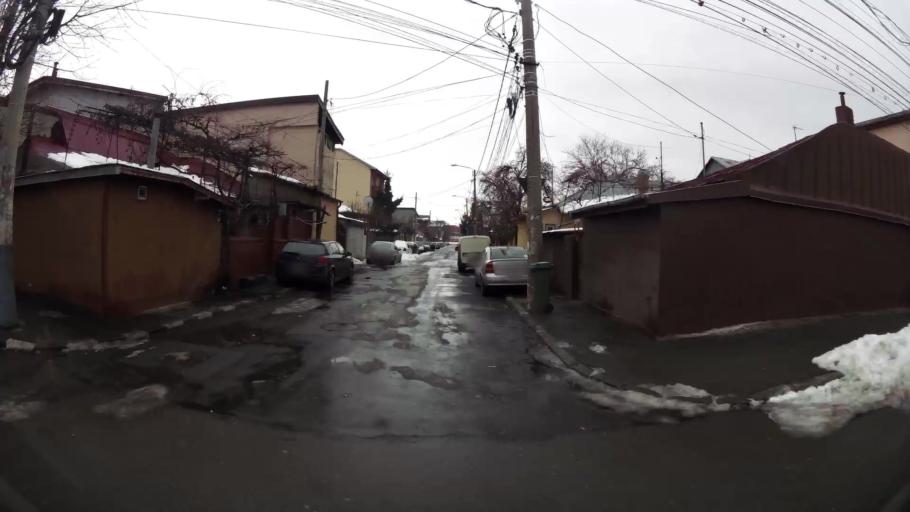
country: RO
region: Ilfov
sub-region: Comuna Pantelimon
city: Pantelimon
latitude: 44.4320
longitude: 26.2042
